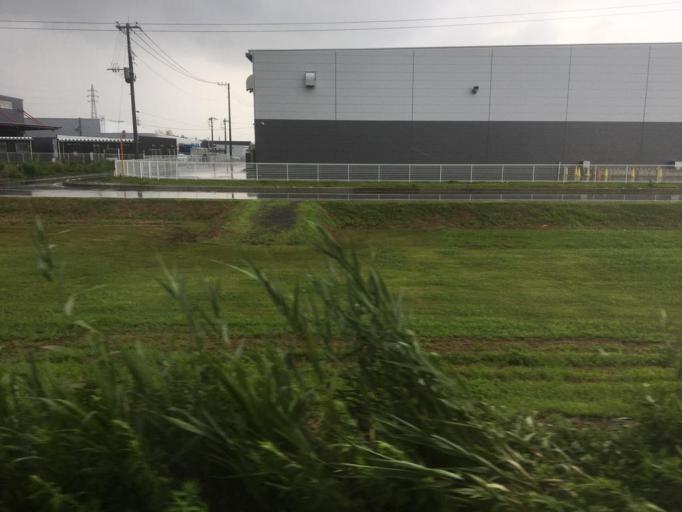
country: JP
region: Tochigi
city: Ashikaga
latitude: 36.2885
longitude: 139.4760
